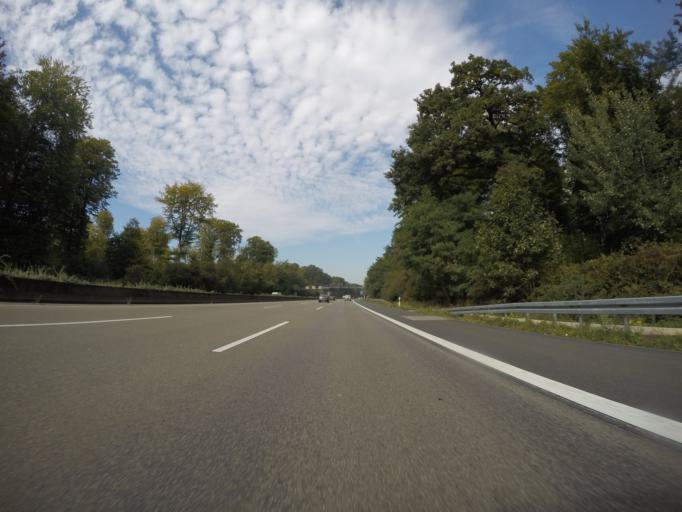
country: DE
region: Hesse
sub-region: Regierungsbezirk Darmstadt
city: Seligenstadt
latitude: 50.0248
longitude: 8.9444
